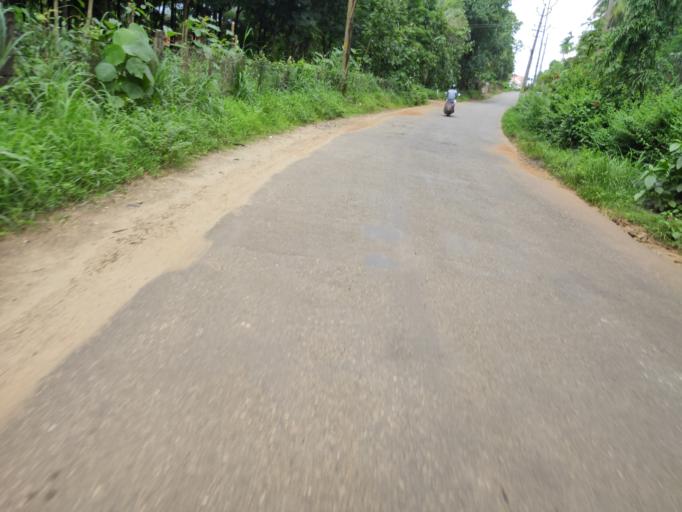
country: IN
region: Kerala
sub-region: Malappuram
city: Manjeri
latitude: 11.2401
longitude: 76.2869
